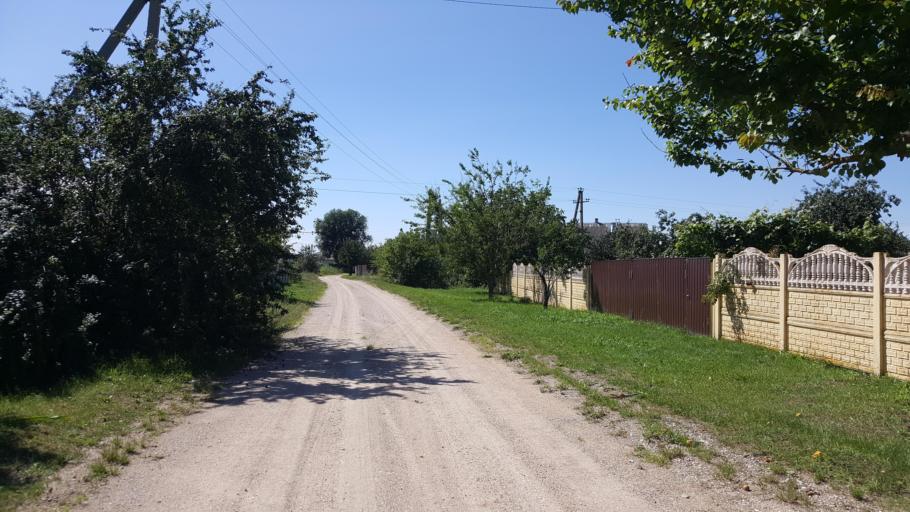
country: BY
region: Brest
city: Charnawchytsy
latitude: 52.2102
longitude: 23.7954
